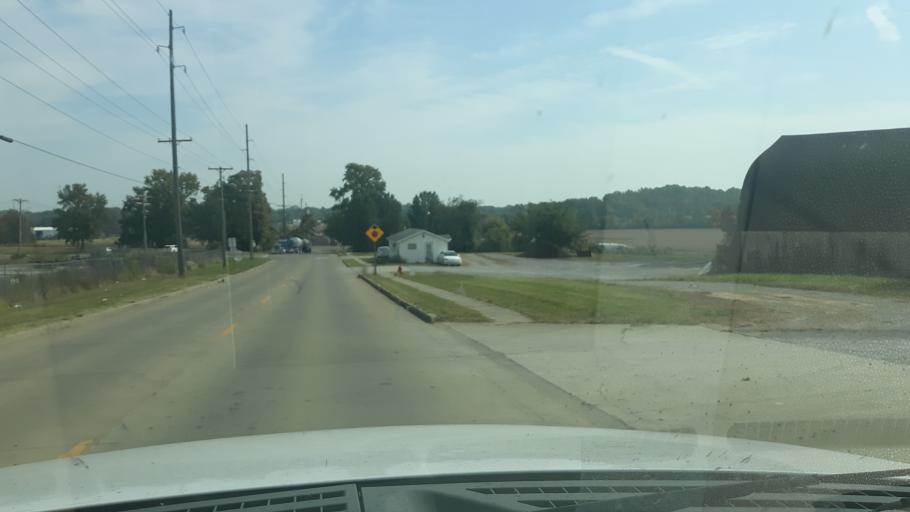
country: US
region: Illinois
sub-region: Saline County
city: Harrisburg
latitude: 37.7203
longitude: -88.5437
